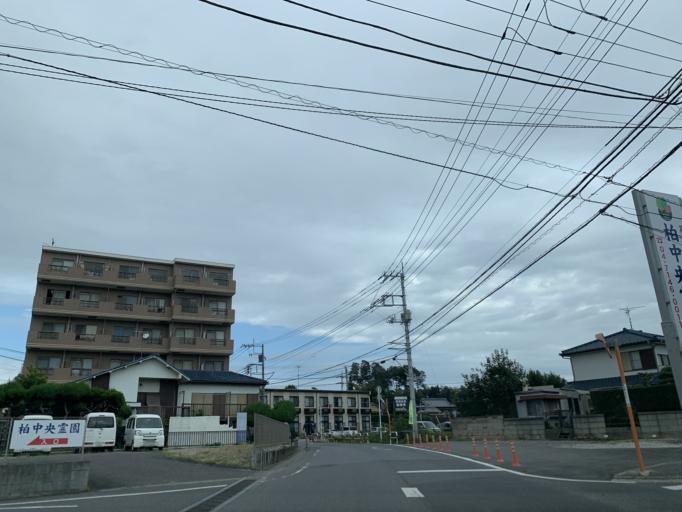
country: JP
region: Chiba
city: Kashiwa
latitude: 35.8752
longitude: 139.9512
